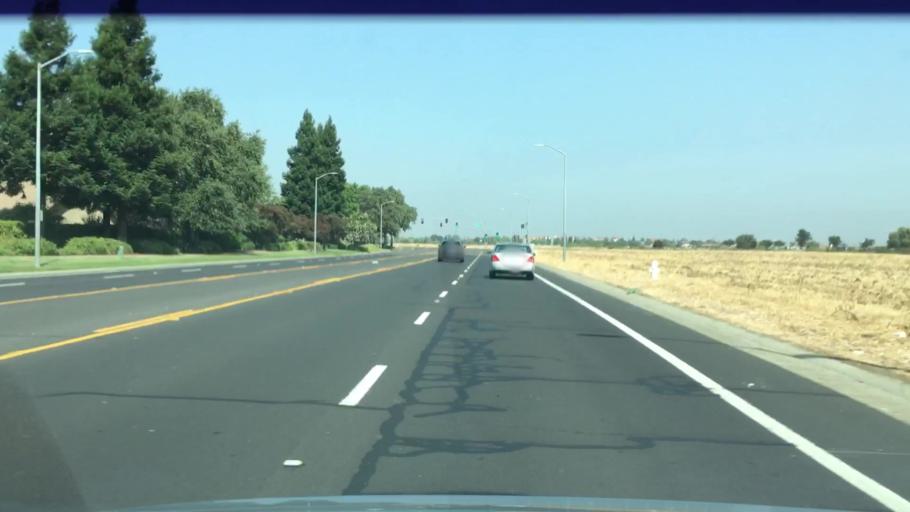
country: US
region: California
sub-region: Sacramento County
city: Laguna
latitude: 38.4276
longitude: -121.4103
